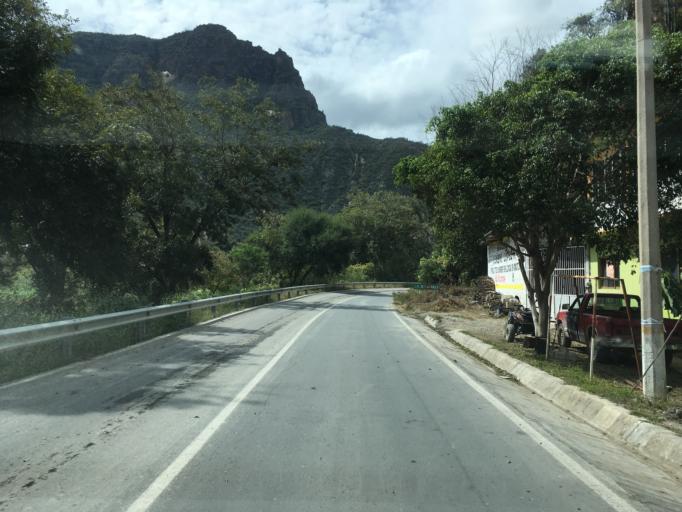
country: MX
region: Hidalgo
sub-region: San Agustin Metzquititlan
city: Mezquititlan
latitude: 20.4997
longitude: -98.7011
